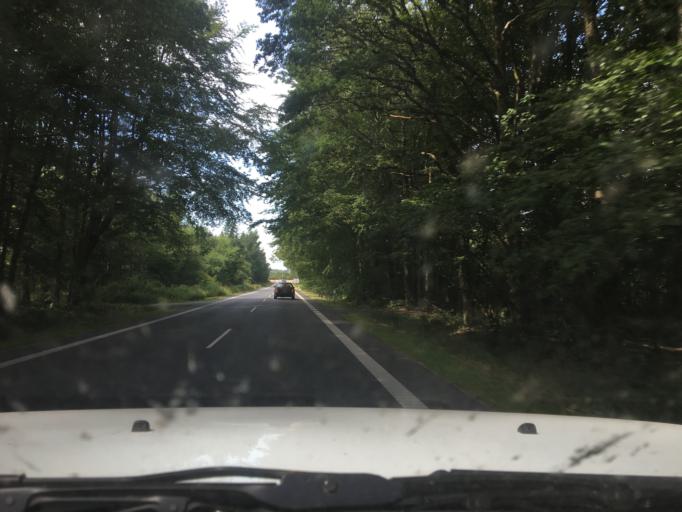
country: DK
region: Central Jutland
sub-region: Viborg Kommune
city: Viborg
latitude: 56.6060
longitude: 9.3560
